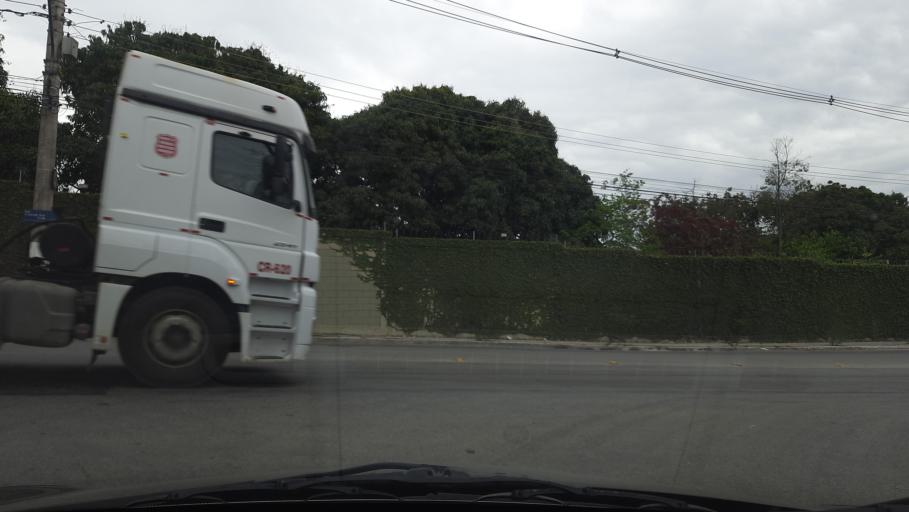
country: BR
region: Sao Paulo
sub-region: Caieiras
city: Caieiras
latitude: -23.4450
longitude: -46.7401
